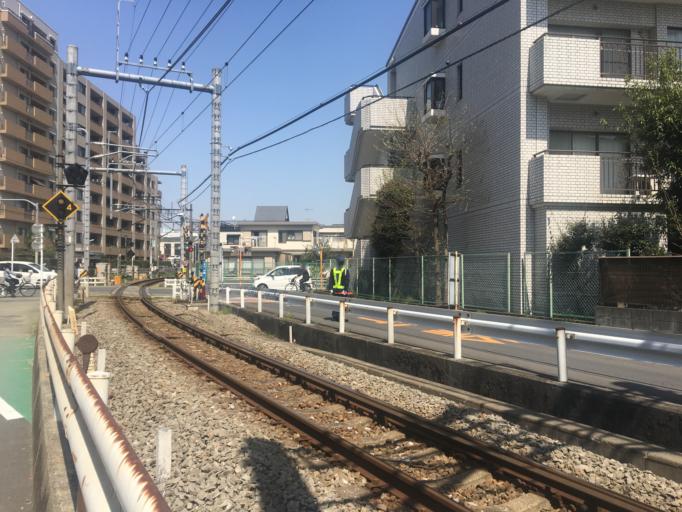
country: JP
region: Tokyo
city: Kokubunji
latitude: 35.7048
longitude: 139.4776
